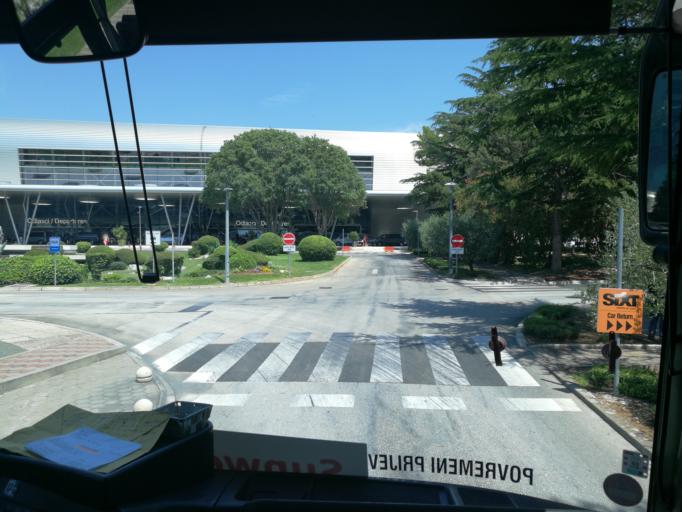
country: HR
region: Dubrovacko-Neretvanska
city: Jasenice
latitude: 42.5592
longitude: 18.2621
